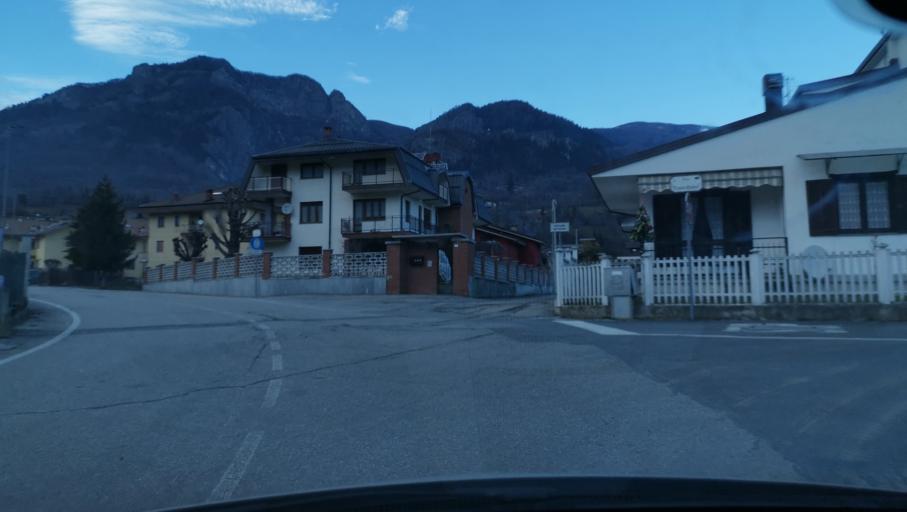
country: IT
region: Piedmont
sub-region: Provincia di Cuneo
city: Demonte
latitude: 44.3175
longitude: 7.2973
